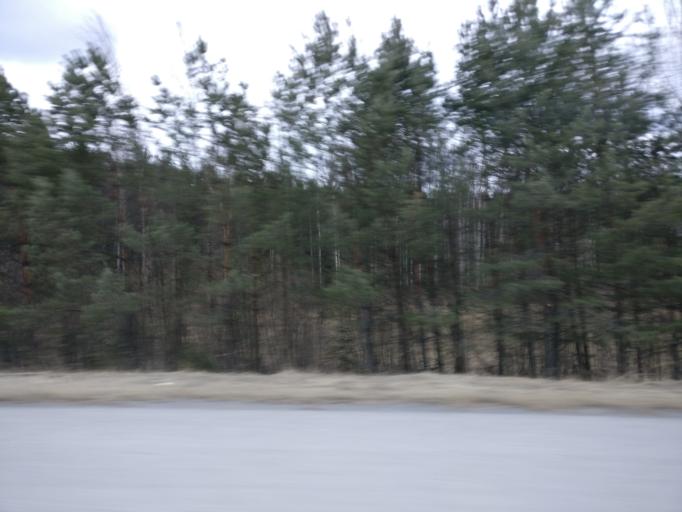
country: FI
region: Haeme
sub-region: Haemeenlinna
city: Janakkala
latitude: 60.8607
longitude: 24.5868
